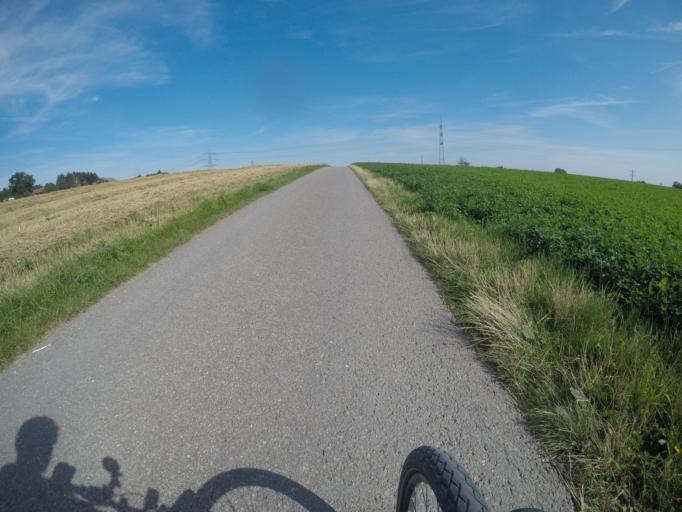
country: DE
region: Baden-Wuerttemberg
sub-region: Karlsruhe Region
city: Wiernsheim
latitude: 48.8973
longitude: 8.8545
